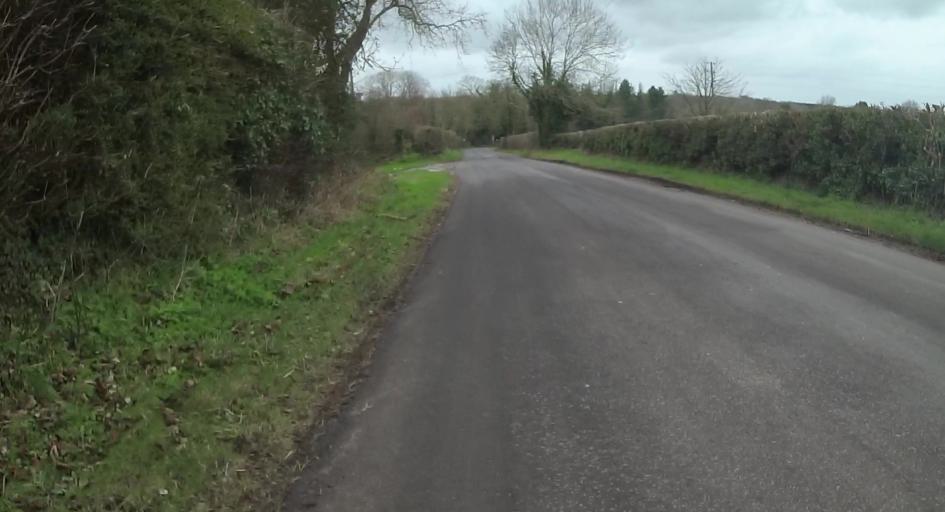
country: GB
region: England
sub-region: Hampshire
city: Kingsclere
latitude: 51.3299
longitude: -1.2807
